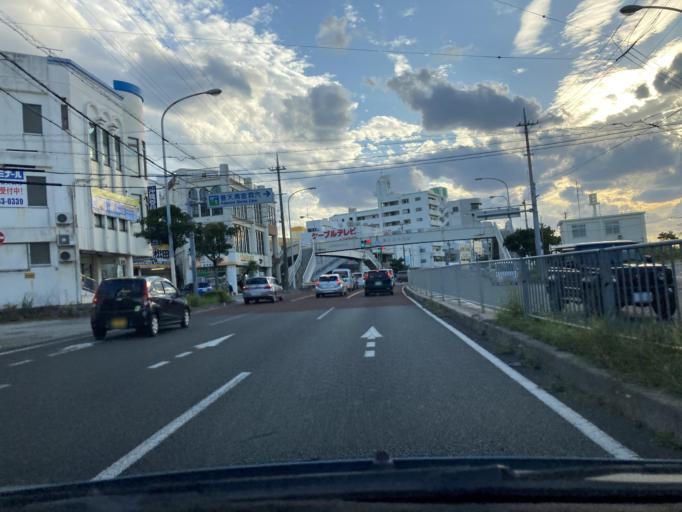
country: JP
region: Okinawa
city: Chatan
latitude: 26.2927
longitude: 127.7777
